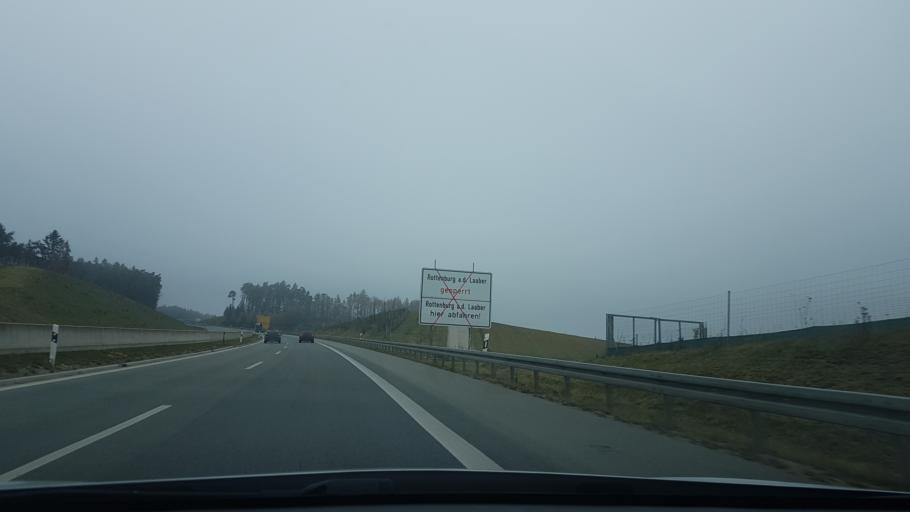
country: DE
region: Bavaria
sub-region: Lower Bavaria
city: Ergoldsbach
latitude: 48.7062
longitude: 12.1771
